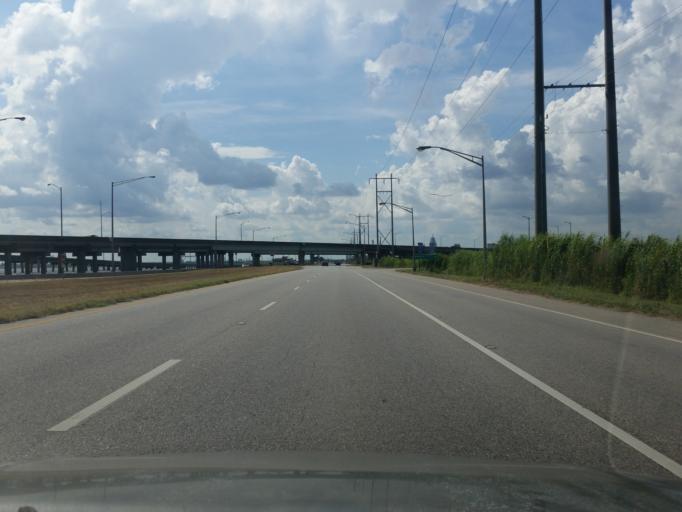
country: US
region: Alabama
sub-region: Mobile County
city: Mobile
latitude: 30.6777
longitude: -87.9839
